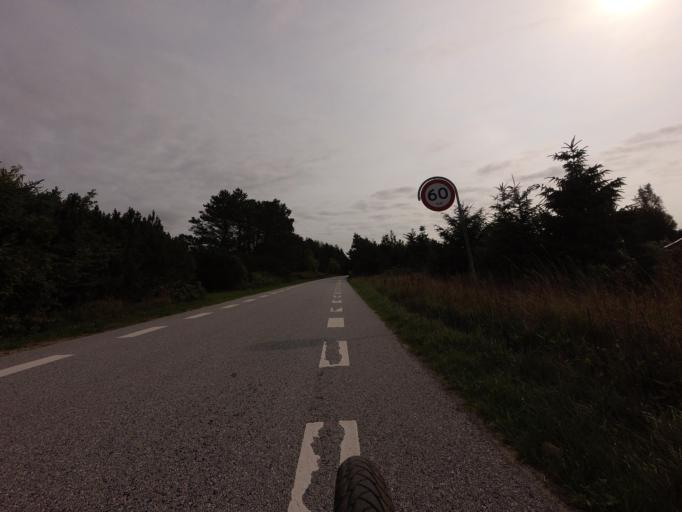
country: DK
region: North Denmark
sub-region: Hjorring Kommune
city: Sindal
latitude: 57.5887
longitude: 10.2024
